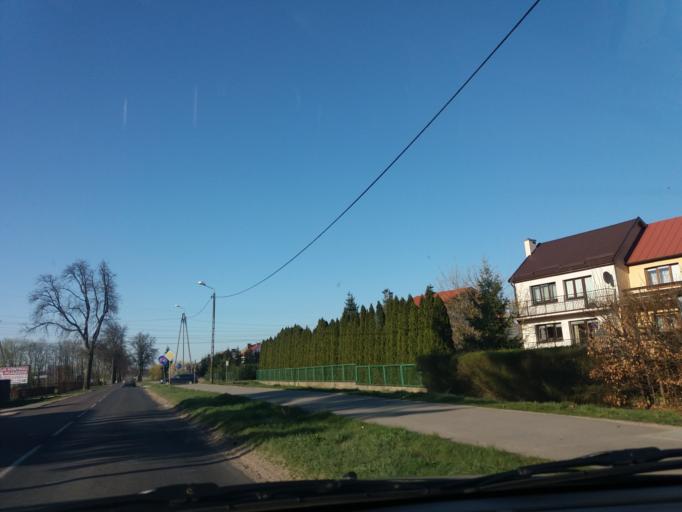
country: PL
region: Warmian-Masurian Voivodeship
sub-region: Powiat nidzicki
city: Nidzica
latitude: 53.3746
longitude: 20.4298
